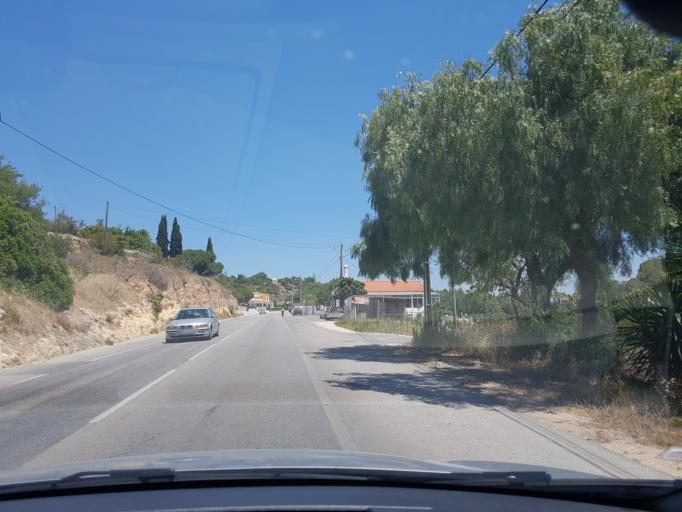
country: PT
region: Faro
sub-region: Lagoa
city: Carvoeiro
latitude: 37.1074
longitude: -8.4621
